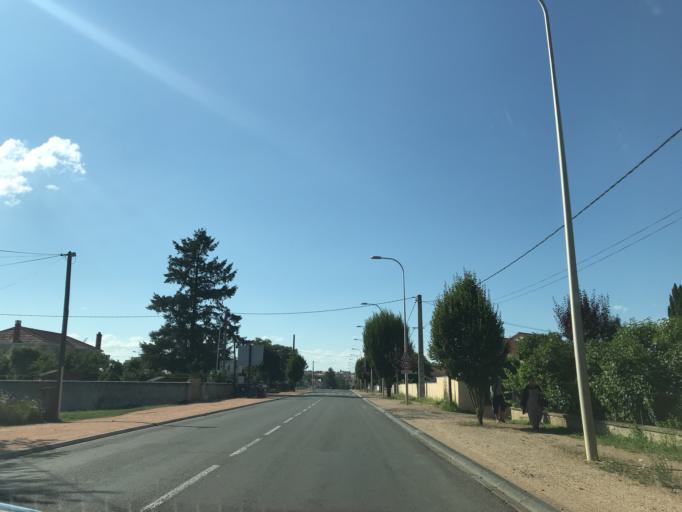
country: FR
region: Auvergne
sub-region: Departement du Puy-de-Dome
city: Pont-du-Chateau
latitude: 45.7903
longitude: 3.2639
